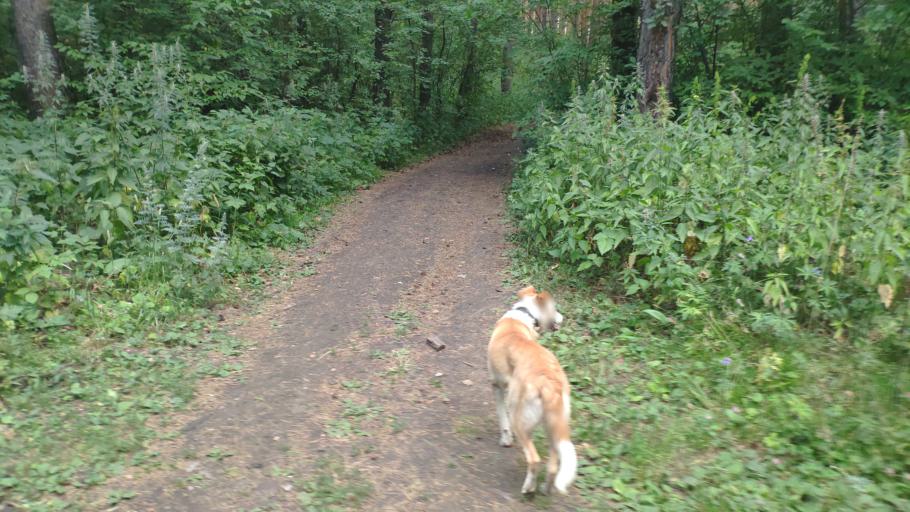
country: RU
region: Bashkortostan
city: Abzakovo
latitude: 53.8088
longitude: 58.6398
